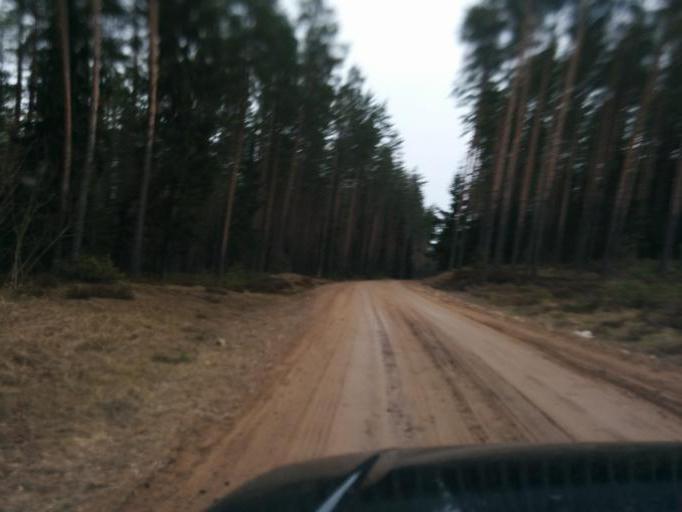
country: LV
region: Ogre
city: Ogre
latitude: 56.7781
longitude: 24.6040
